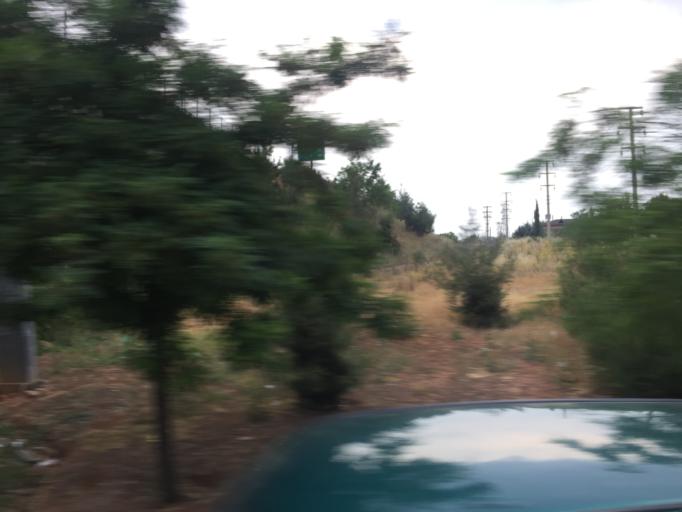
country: TR
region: Gaziantep
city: Gaziantep
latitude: 37.0196
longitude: 37.4291
